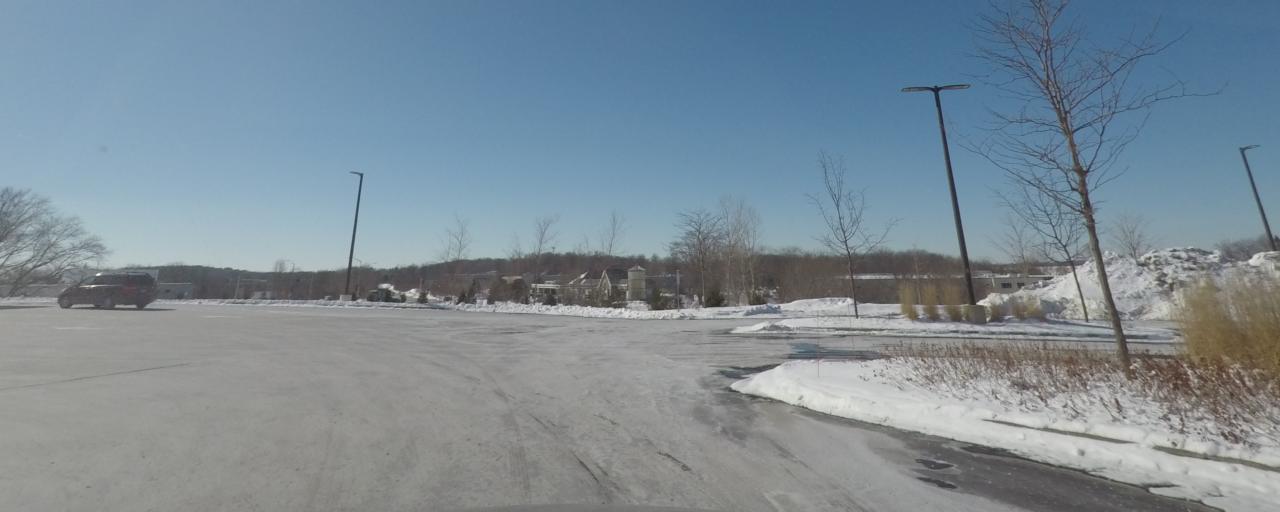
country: US
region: Wisconsin
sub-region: Waukesha County
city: New Berlin
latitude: 42.9454
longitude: -88.1072
